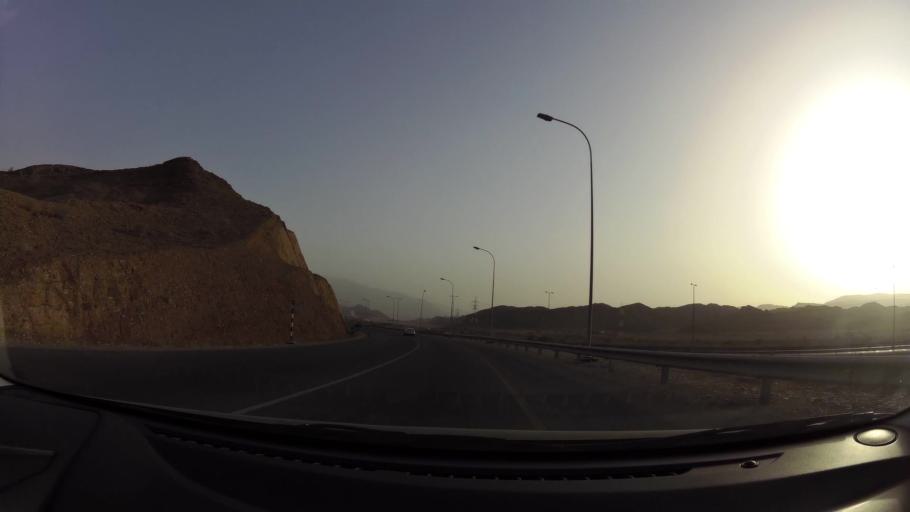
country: OM
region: Muhafazat Masqat
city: Bawshar
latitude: 23.5185
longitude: 58.3476
